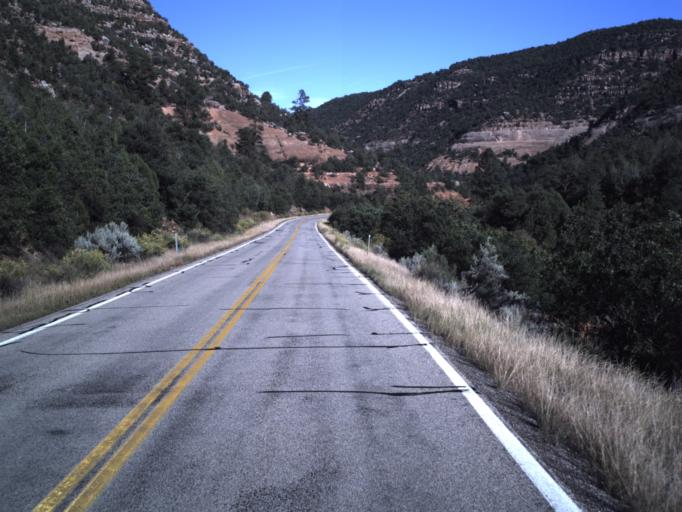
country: US
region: Utah
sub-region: San Juan County
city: Monticello
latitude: 38.3280
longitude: -109.0731
